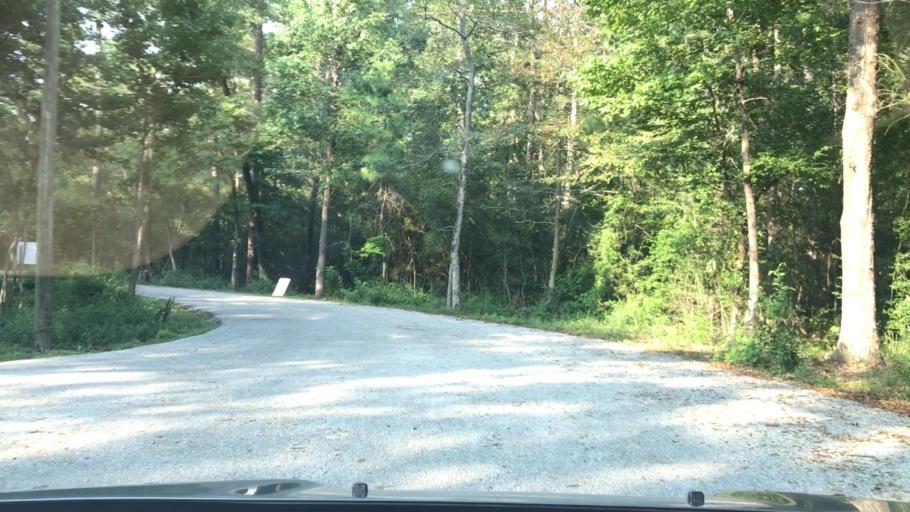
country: US
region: Texas
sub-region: Walker County
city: Huntsville
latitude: 30.6352
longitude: -95.5143
